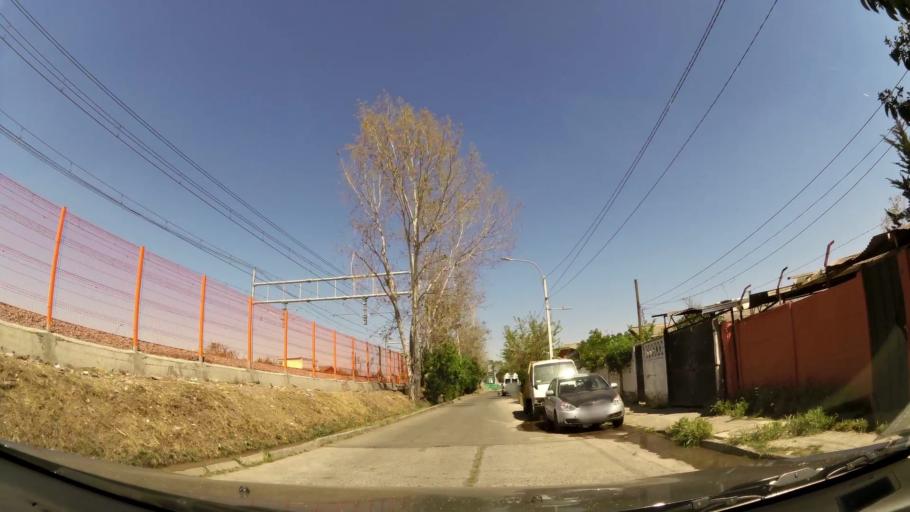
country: CL
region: Santiago Metropolitan
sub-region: Provincia de Maipo
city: San Bernardo
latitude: -33.5809
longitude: -70.6991
